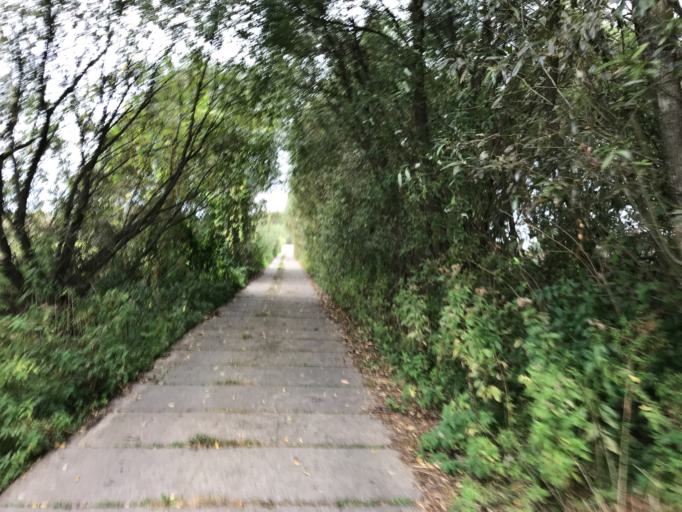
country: PL
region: Podlasie
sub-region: Powiat bialostocki
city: Choroszcz
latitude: 53.1382
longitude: 22.8723
